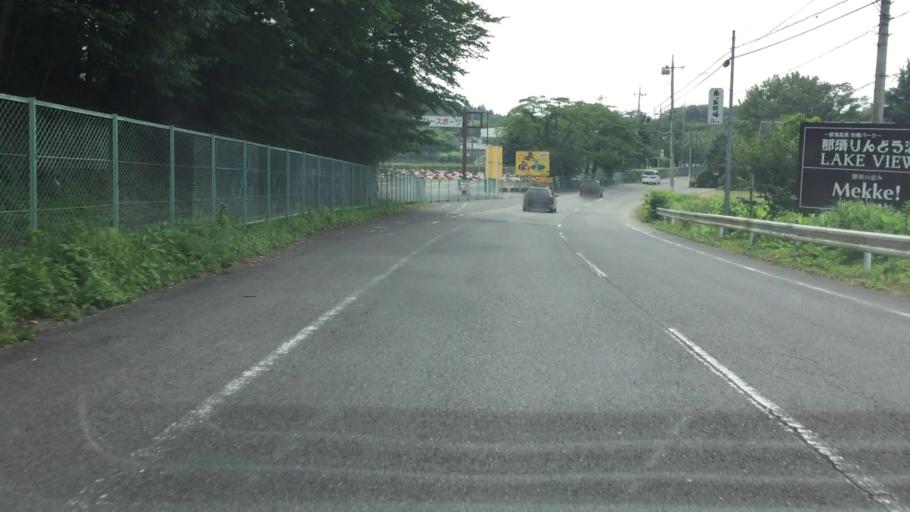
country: JP
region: Tochigi
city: Kuroiso
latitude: 37.0429
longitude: 140.0447
